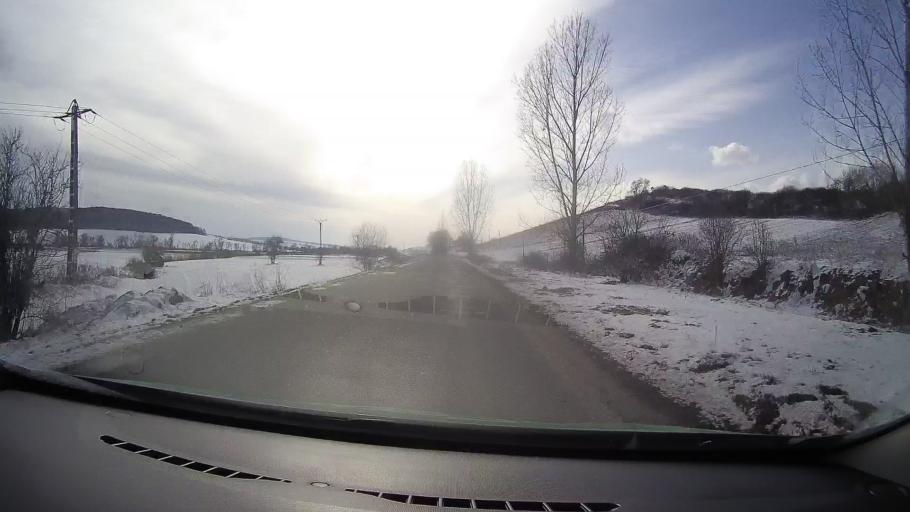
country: RO
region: Sibiu
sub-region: Comuna Iacobeni
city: Iacobeni
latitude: 46.0386
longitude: 24.7285
